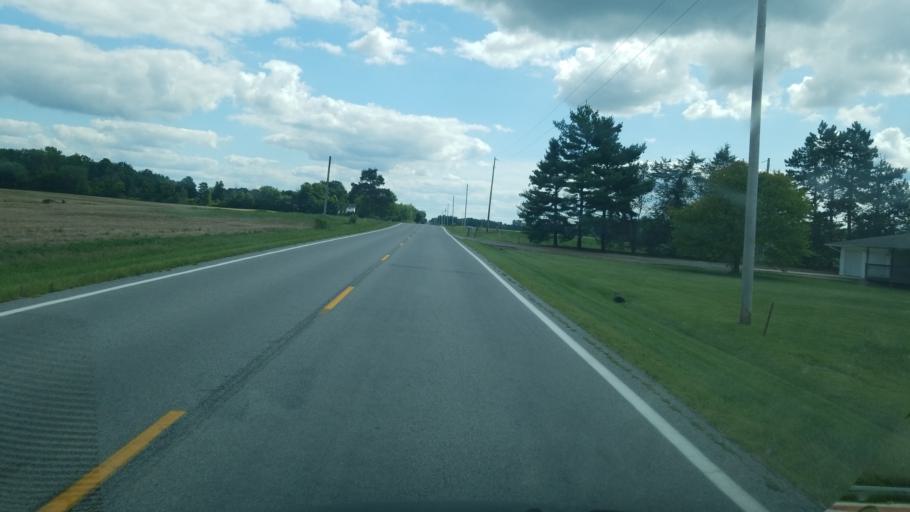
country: US
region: Ohio
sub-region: Allen County
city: Lima
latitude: 40.6775
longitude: -83.9758
